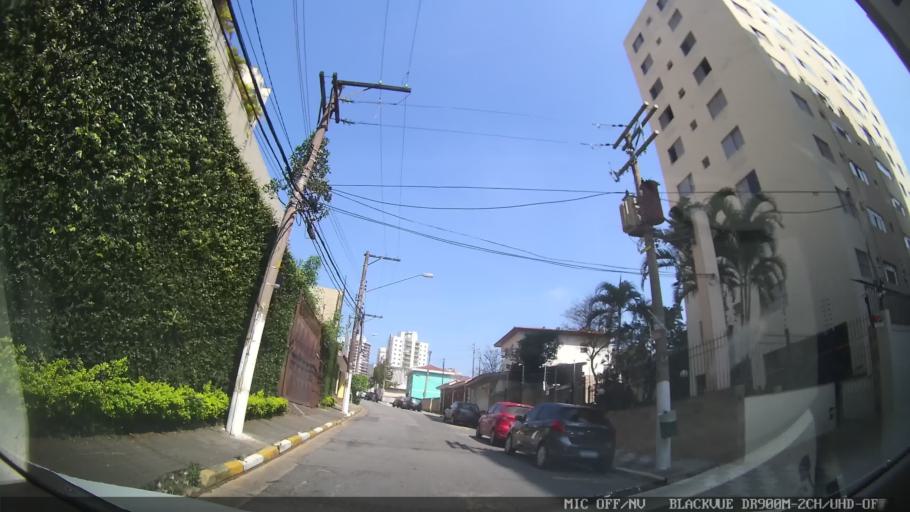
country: BR
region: Sao Paulo
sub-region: Sao Paulo
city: Sao Paulo
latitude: -23.4871
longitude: -46.6324
